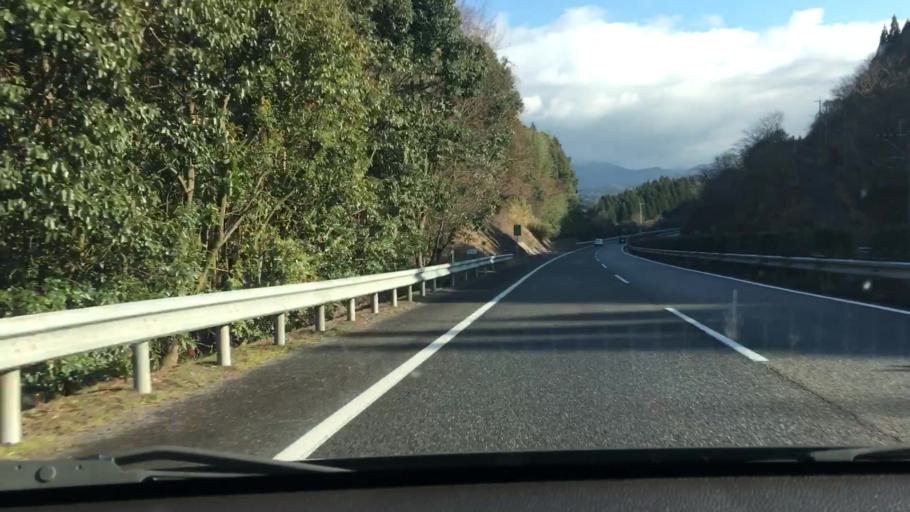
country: JP
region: Kumamoto
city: Hitoyoshi
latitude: 32.1800
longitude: 130.7851
